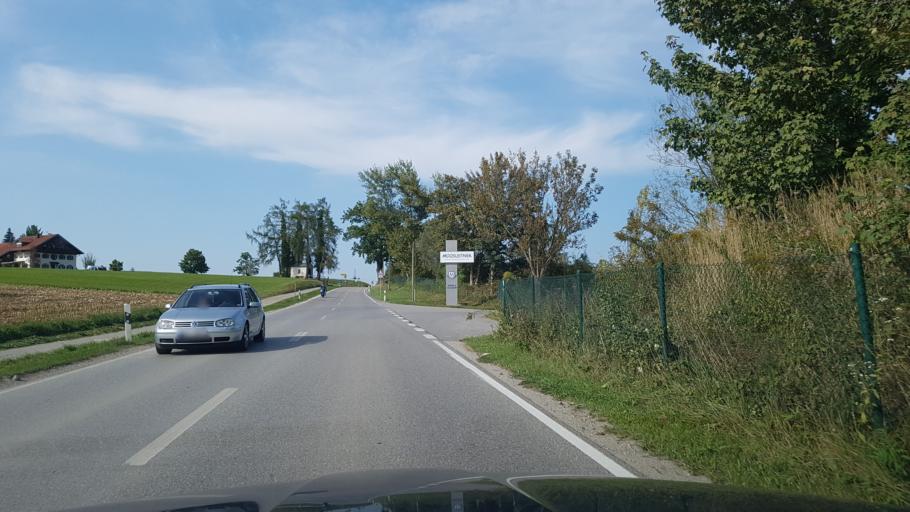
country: DE
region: Bavaria
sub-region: Upper Bavaria
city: Laufen
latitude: 47.8807
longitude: 12.9263
